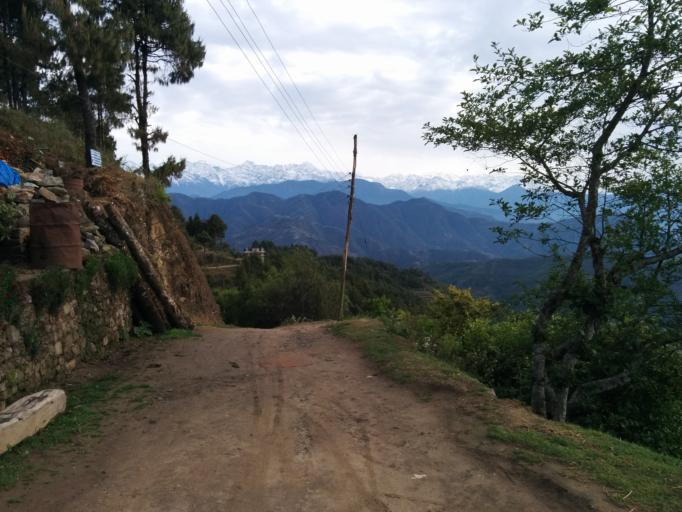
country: NP
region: Central Region
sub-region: Bagmati Zone
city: Nagarkot
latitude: 27.8259
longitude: 85.4486
